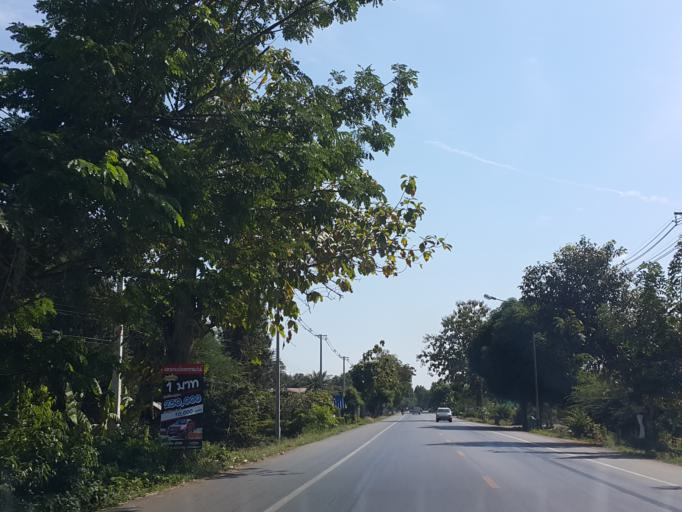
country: TH
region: Sukhothai
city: Sawankhalok
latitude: 17.2572
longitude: 99.8522
